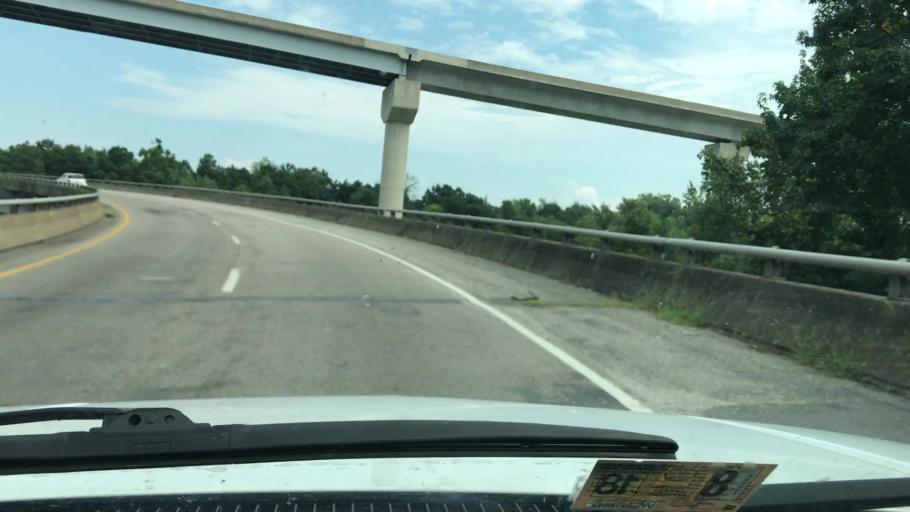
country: US
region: Virginia
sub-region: Chesterfield County
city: Bensley
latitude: 37.4413
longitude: -77.4278
